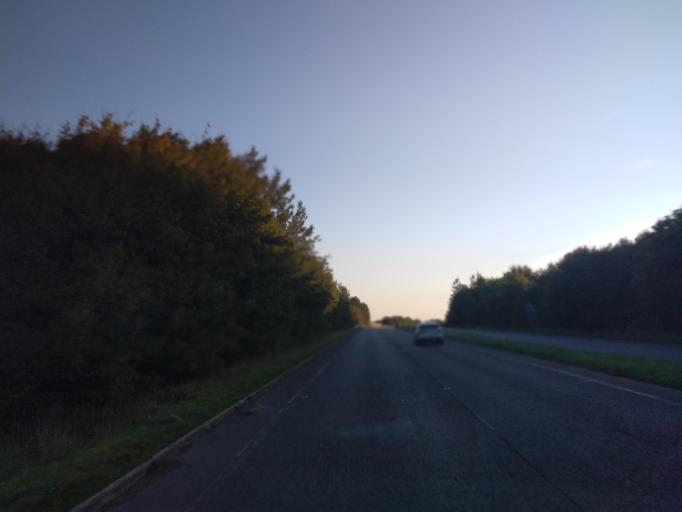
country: GB
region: England
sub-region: West Sussex
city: Littlehampton
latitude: 50.8222
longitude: -0.5238
